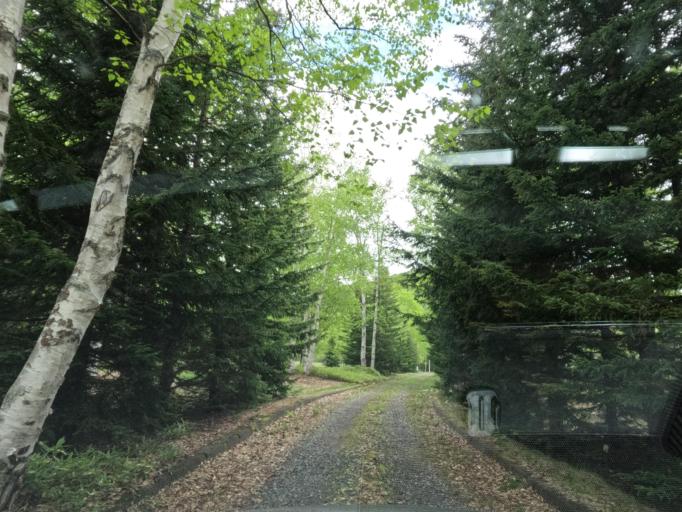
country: JP
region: Hokkaido
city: Kamikawa
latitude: 43.6439
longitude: 143.0223
